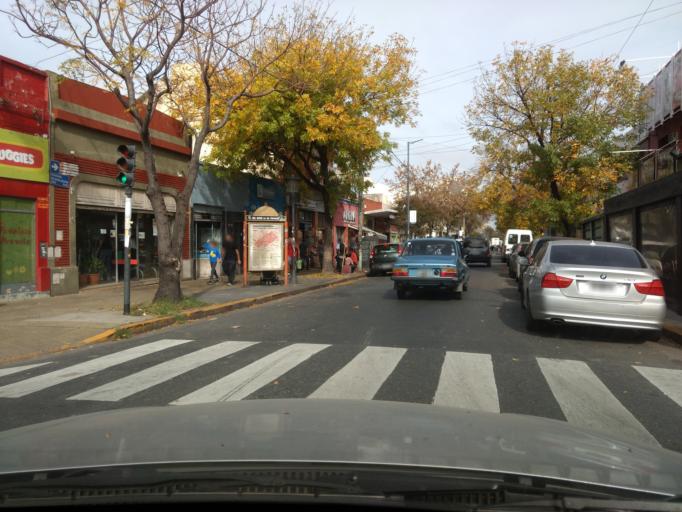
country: AR
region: Buenos Aires F.D.
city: Villa Santa Rita
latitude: -34.6208
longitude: -58.5077
